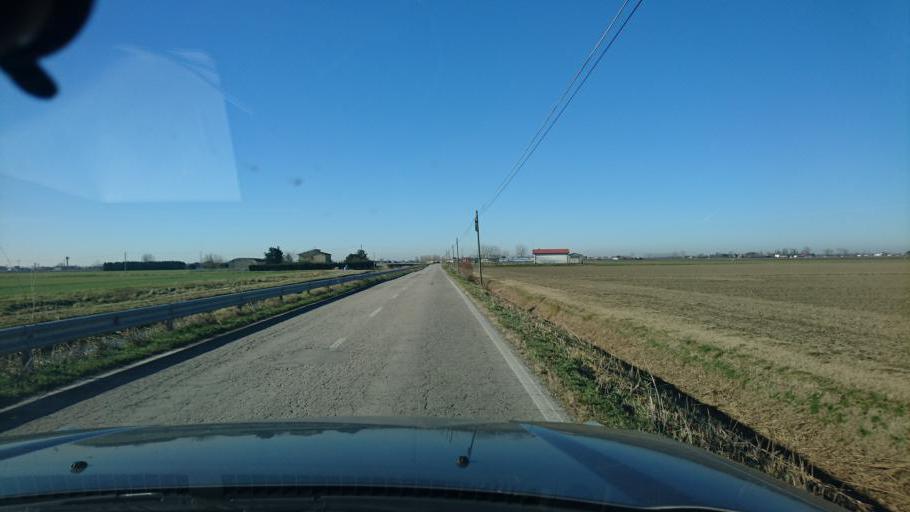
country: IT
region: Emilia-Romagna
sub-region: Provincia di Ferrara
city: Mesola
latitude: 44.9446
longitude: 12.2437
